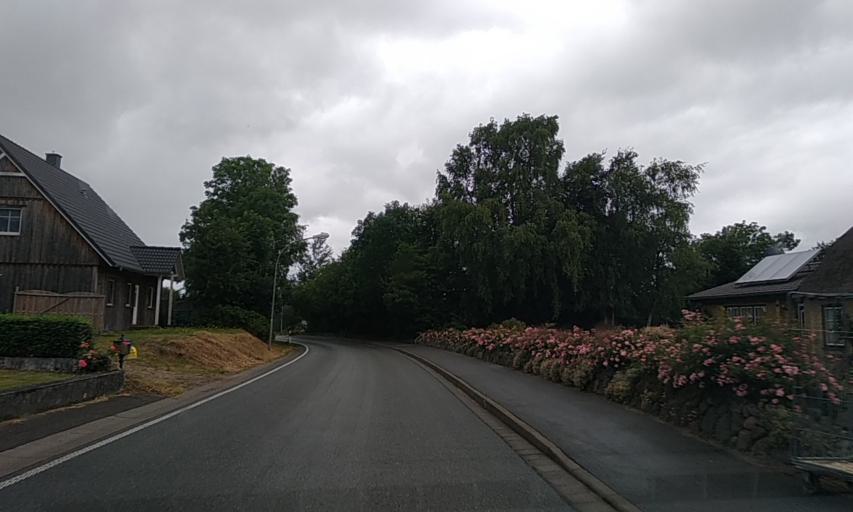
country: DE
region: Schleswig-Holstein
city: Neuberend
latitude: 54.5513
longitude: 9.5168
